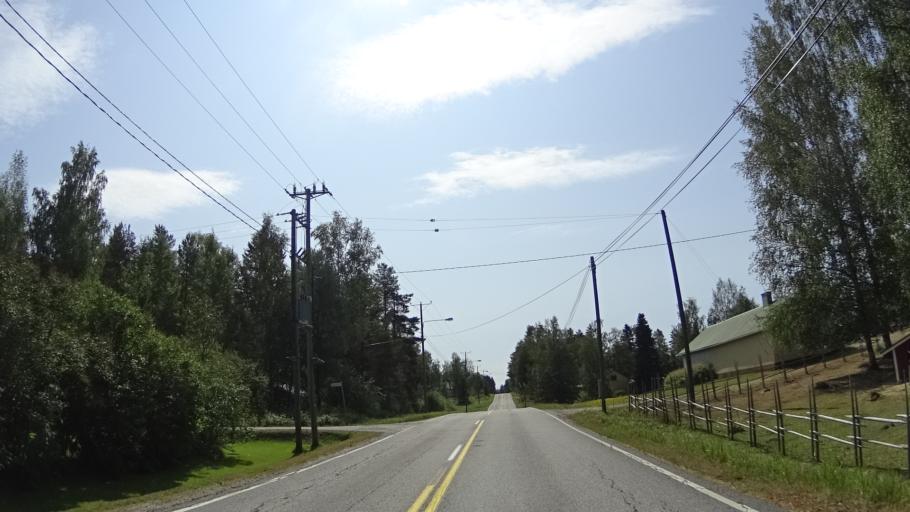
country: FI
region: Pirkanmaa
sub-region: Ylae-Pirkanmaa
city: Maenttae
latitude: 61.8927
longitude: 24.7928
